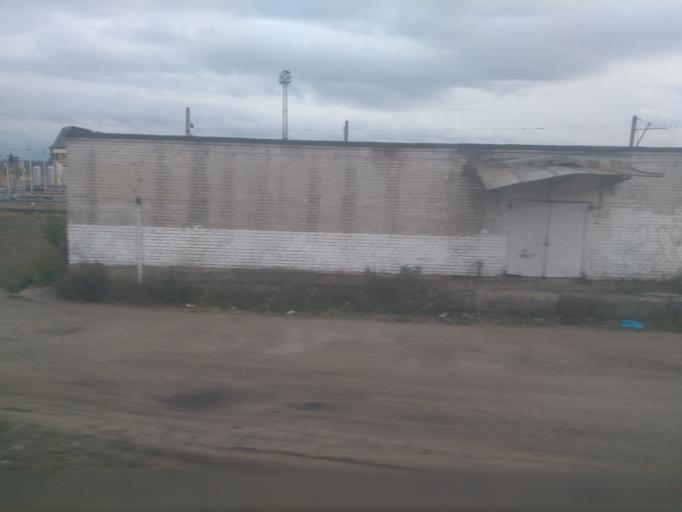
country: RU
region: Tatarstan
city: Osinovo
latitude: 55.8168
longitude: 48.9021
